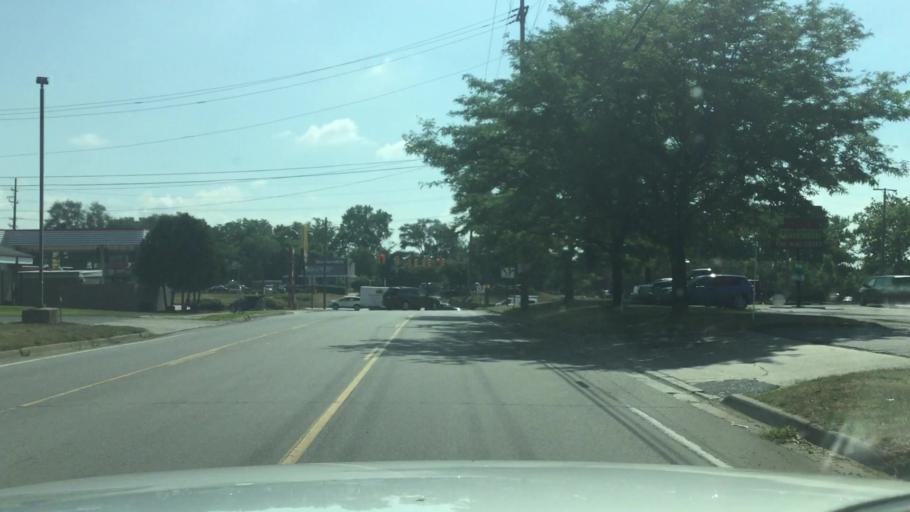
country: US
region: Michigan
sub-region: Wayne County
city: Belleville
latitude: 42.2137
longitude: -83.5451
